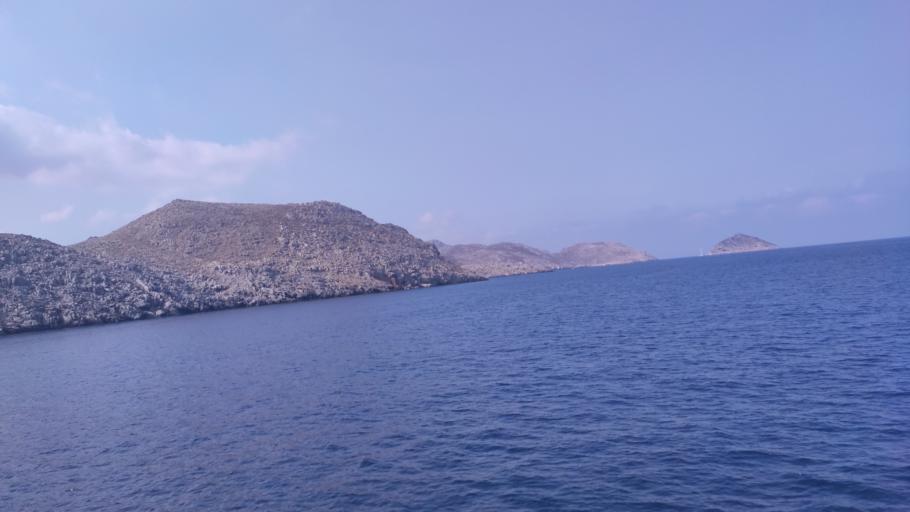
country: GR
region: South Aegean
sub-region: Nomos Dodekanisou
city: Symi
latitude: 36.6445
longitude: 27.8225
